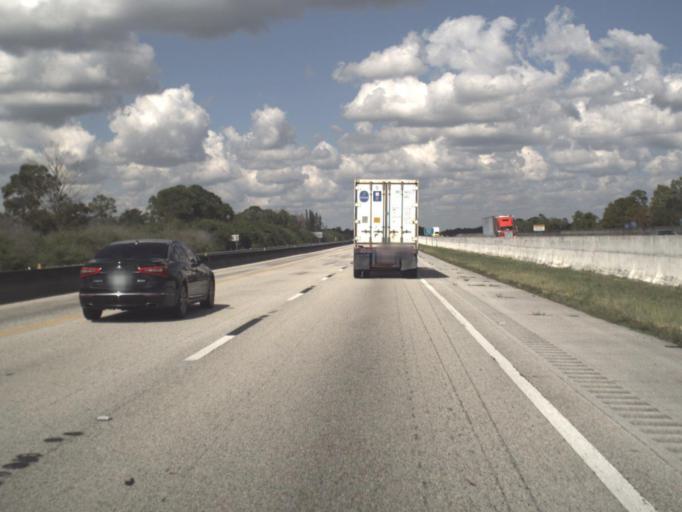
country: US
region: Florida
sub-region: Palm Beach County
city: Limestone Creek
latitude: 26.9556
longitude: -80.1663
